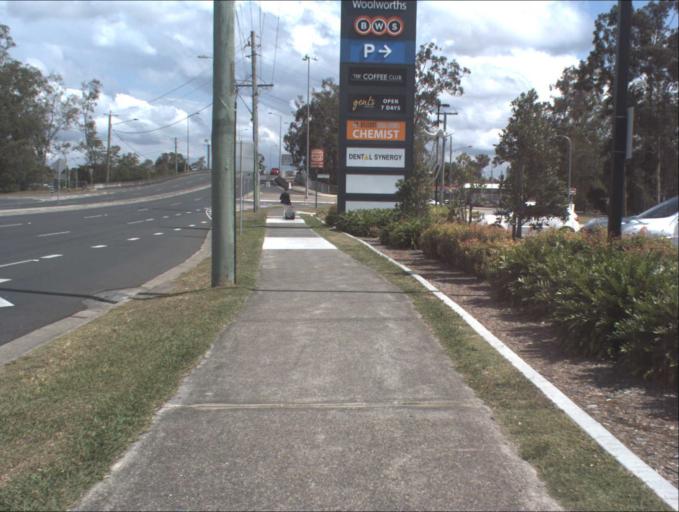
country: AU
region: Queensland
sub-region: Logan
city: Slacks Creek
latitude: -27.6690
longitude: 153.1392
